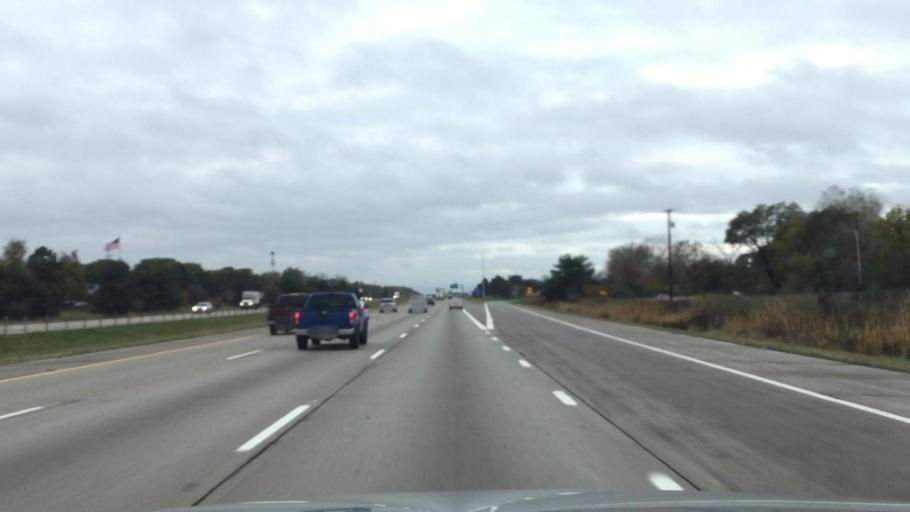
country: US
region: Michigan
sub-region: Wayne County
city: Belleville
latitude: 42.2193
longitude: -83.5127
